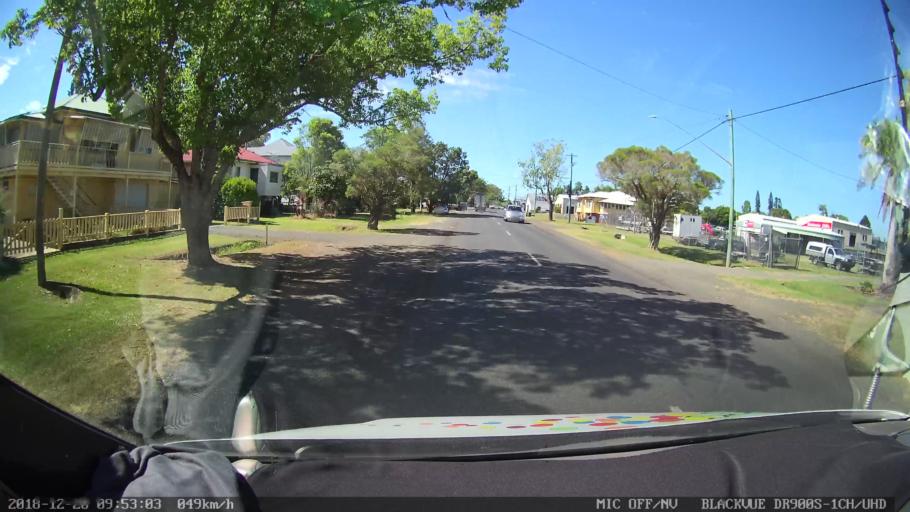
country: AU
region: New South Wales
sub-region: Lismore Municipality
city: Lismore
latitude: -28.7999
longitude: 153.2701
